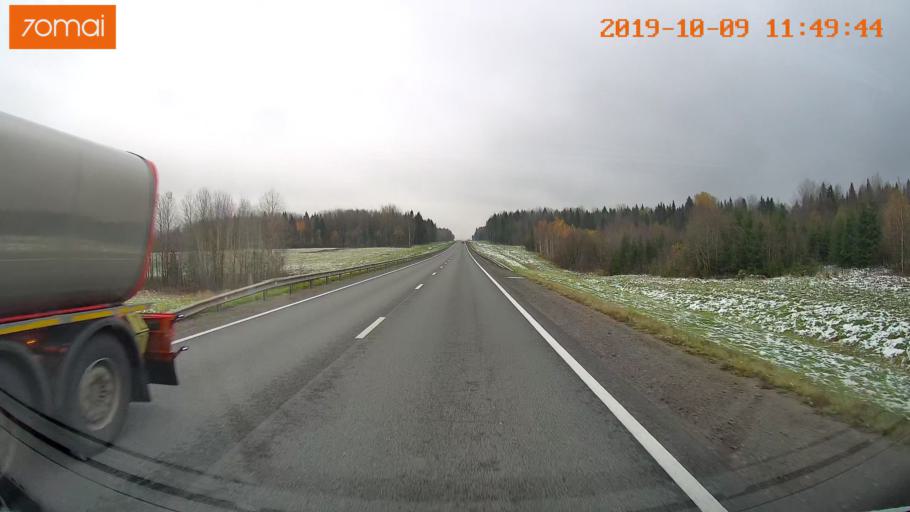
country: RU
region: Vologda
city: Gryazovets
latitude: 58.8148
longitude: 40.2348
